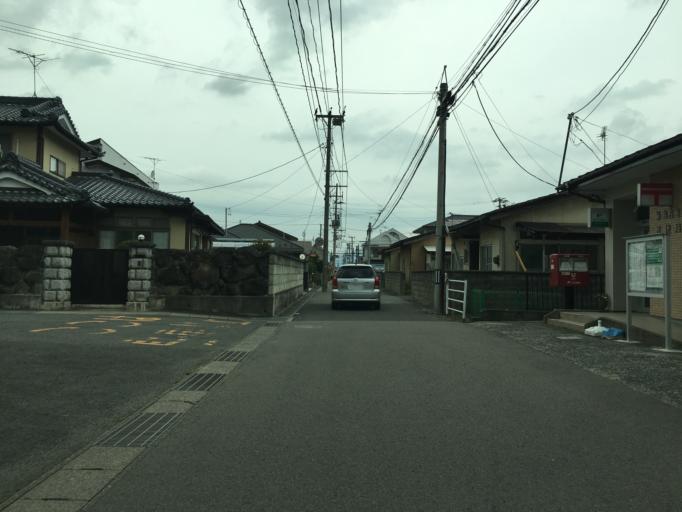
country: JP
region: Fukushima
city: Fukushima-shi
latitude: 37.7433
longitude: 140.4412
